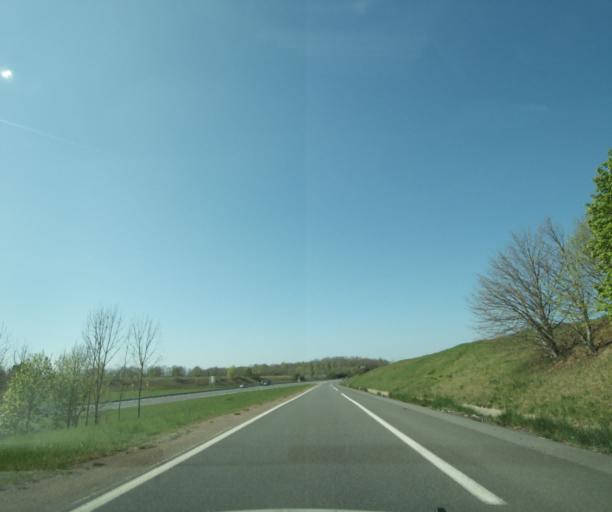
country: FR
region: Bourgogne
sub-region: Departement de la Nievre
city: Pouilly-sur-Loire
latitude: 47.3418
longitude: 2.9292
